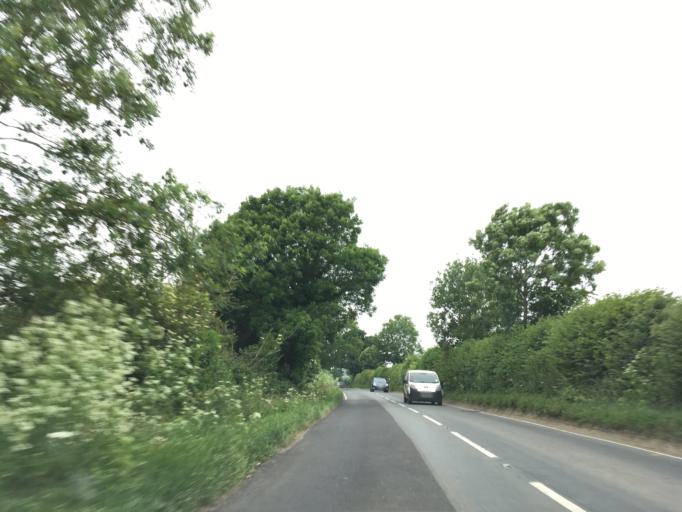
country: GB
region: England
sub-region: Gloucestershire
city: Stonehouse
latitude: 51.7629
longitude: -2.3466
